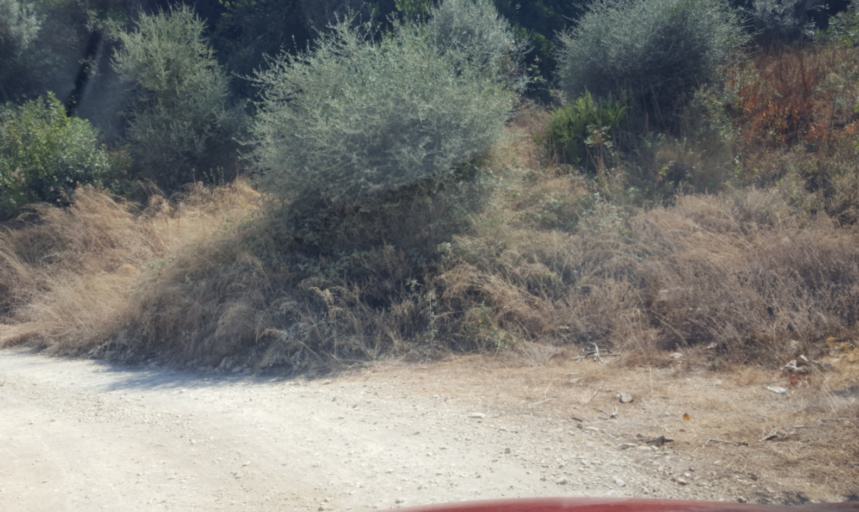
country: GR
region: Ionian Islands
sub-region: Lefkada
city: Nidri
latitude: 38.6635
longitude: 20.7138
